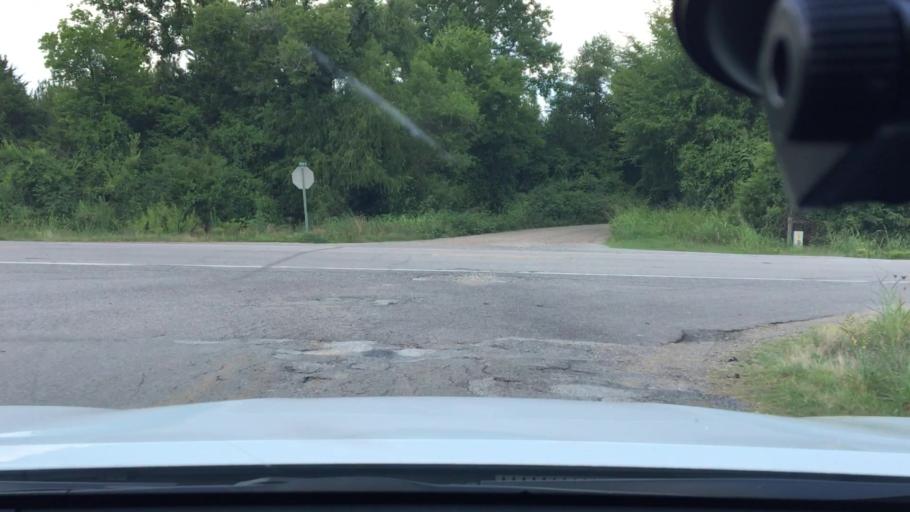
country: US
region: Arkansas
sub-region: Logan County
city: Paris
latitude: 35.2680
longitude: -93.6830
